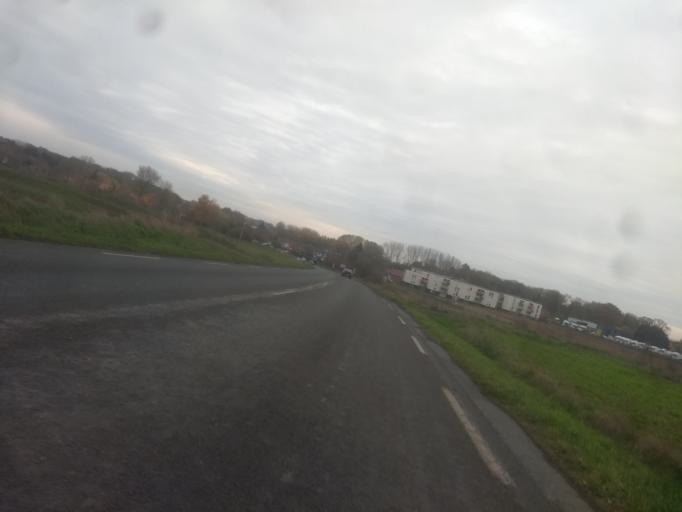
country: FR
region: Nord-Pas-de-Calais
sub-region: Departement du Pas-de-Calais
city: Achicourt
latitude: 50.2686
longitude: 2.7493
